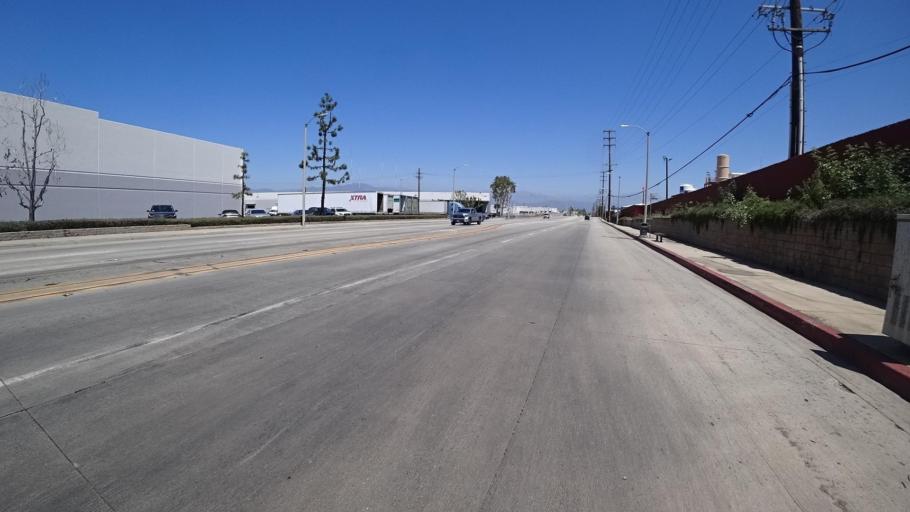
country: US
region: California
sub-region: Los Angeles County
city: Avocado Heights
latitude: 34.0246
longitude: -117.9847
